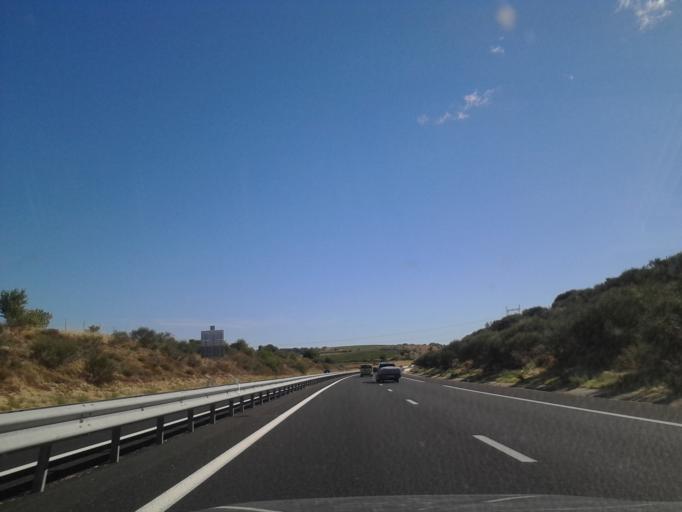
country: FR
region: Languedoc-Roussillon
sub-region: Departement de l'Herault
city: Paulhan
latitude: 43.5472
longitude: 3.4484
